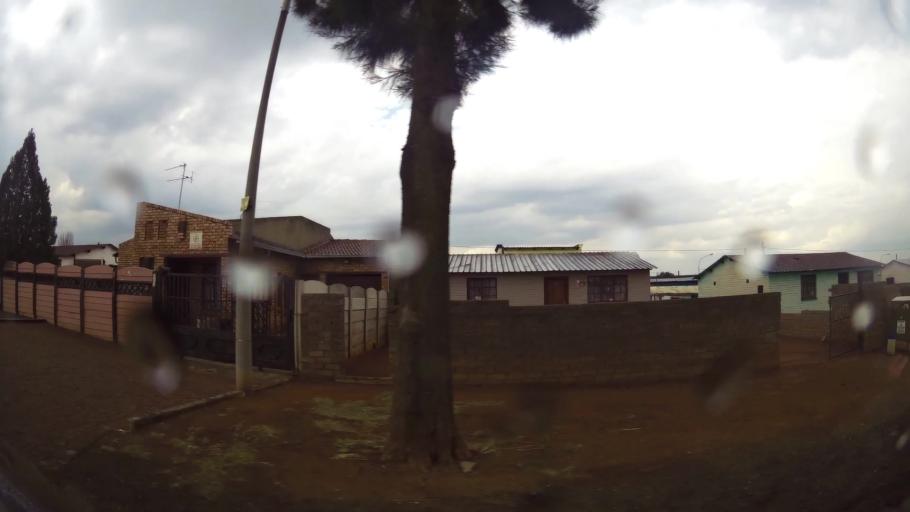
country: ZA
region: Gauteng
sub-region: Ekurhuleni Metropolitan Municipality
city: Germiston
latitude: -26.3784
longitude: 28.1309
